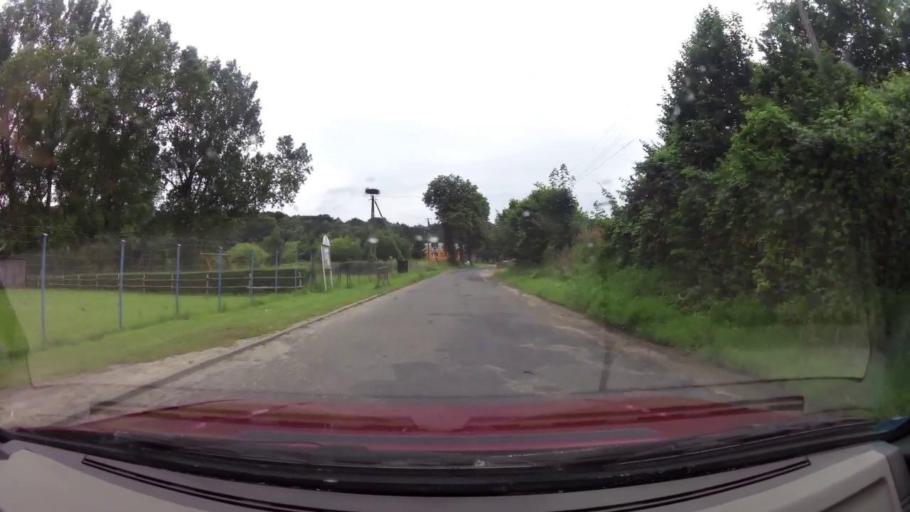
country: PL
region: West Pomeranian Voivodeship
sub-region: Powiat bialogardzki
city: Bialogard
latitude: 53.9476
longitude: 15.9594
